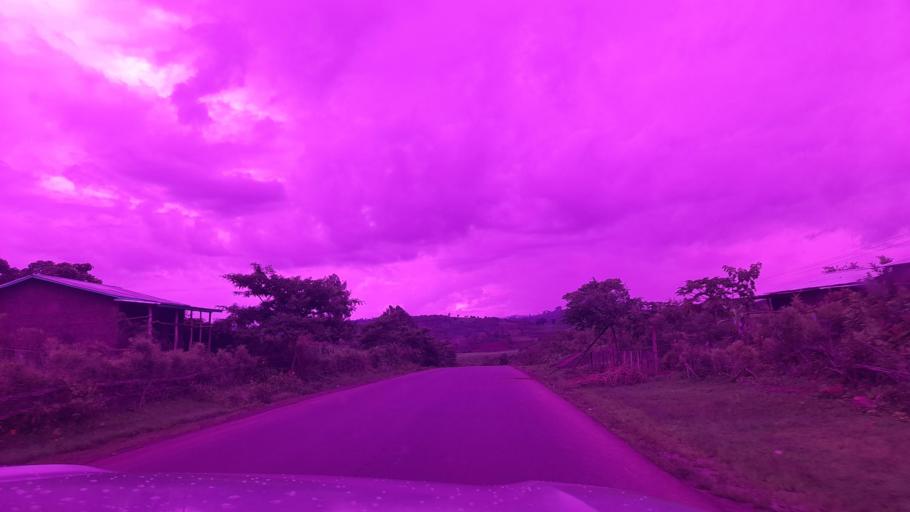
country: ET
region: Oromiya
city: Jima
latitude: 7.7673
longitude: 37.3400
